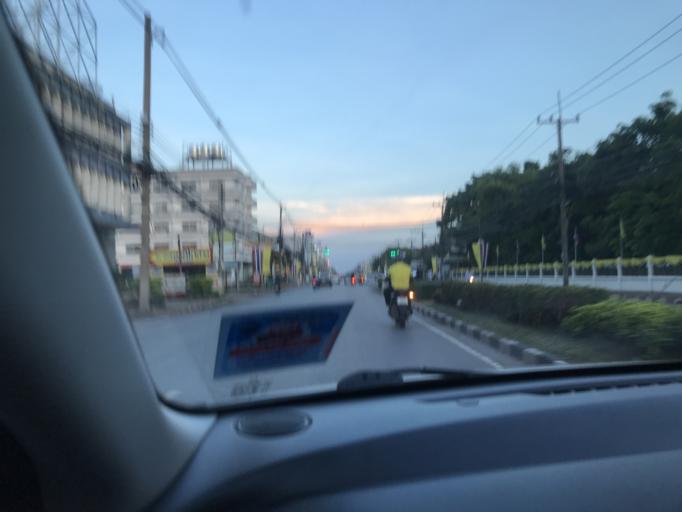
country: TH
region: Changwat Udon Thani
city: Udon Thani
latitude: 17.3960
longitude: 102.7969
